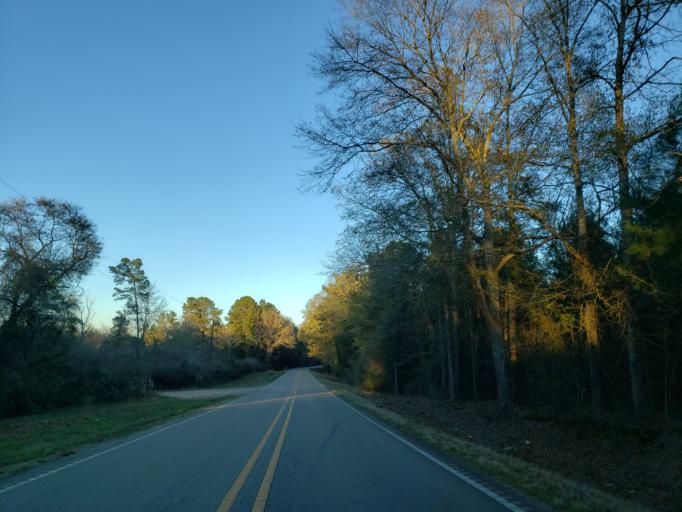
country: US
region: Mississippi
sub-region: Covington County
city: Collins
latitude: 31.5612
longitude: -89.4426
